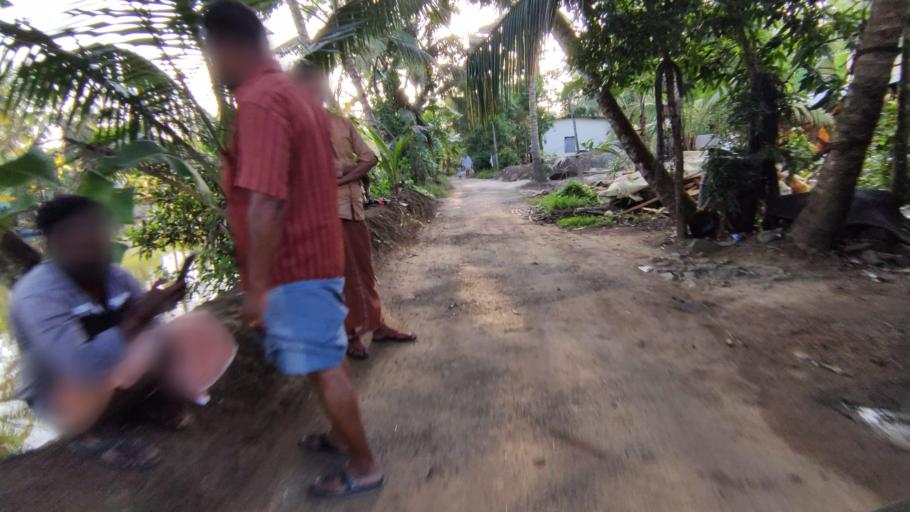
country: IN
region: Kerala
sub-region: Kottayam
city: Kottayam
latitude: 9.5759
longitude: 76.4507
